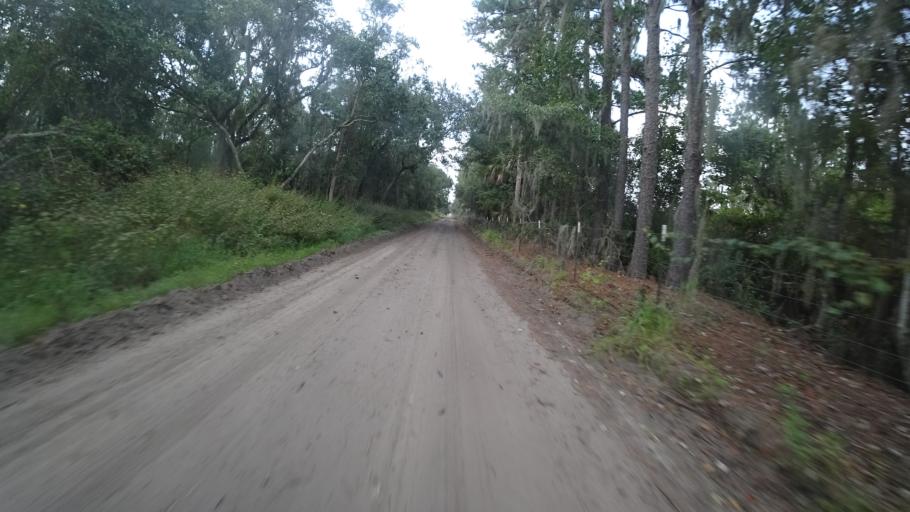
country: US
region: Florida
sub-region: Hillsborough County
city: Wimauma
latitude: 27.6056
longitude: -82.1329
